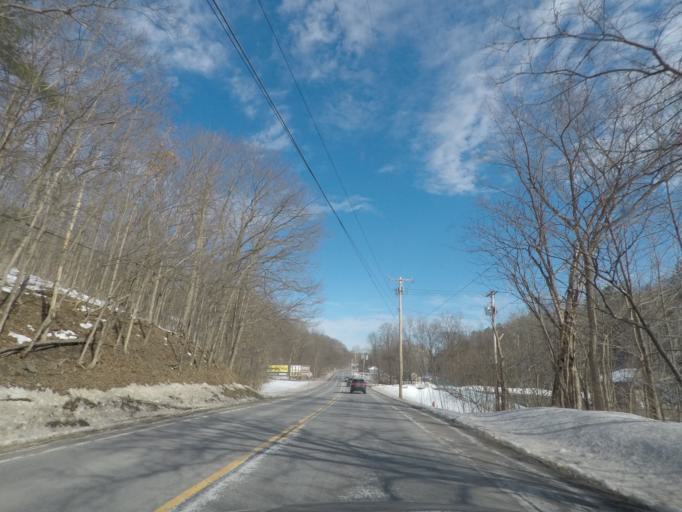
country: US
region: New York
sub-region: Albany County
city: Altamont
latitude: 42.7786
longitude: -74.0659
